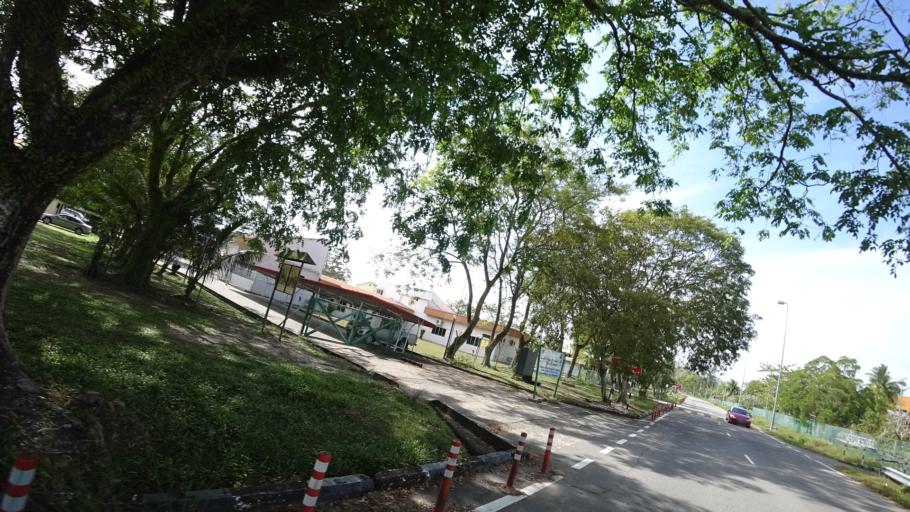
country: BN
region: Tutong
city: Tutong
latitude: 4.8180
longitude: 114.6638
